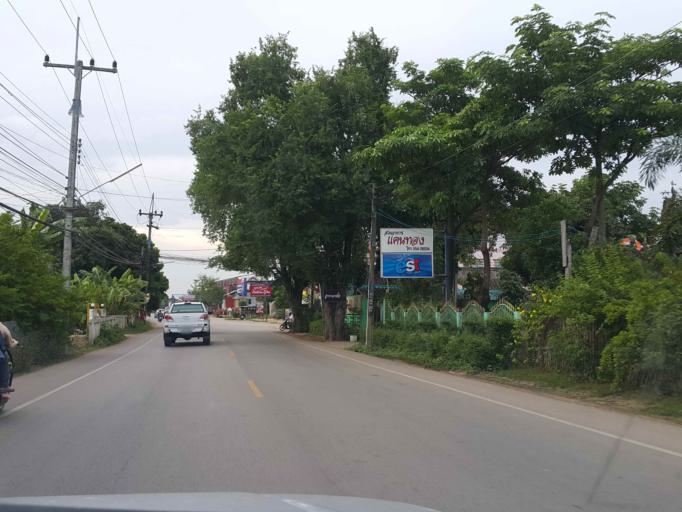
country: TH
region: Lampang
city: Ko Kha
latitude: 18.1998
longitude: 99.3907
